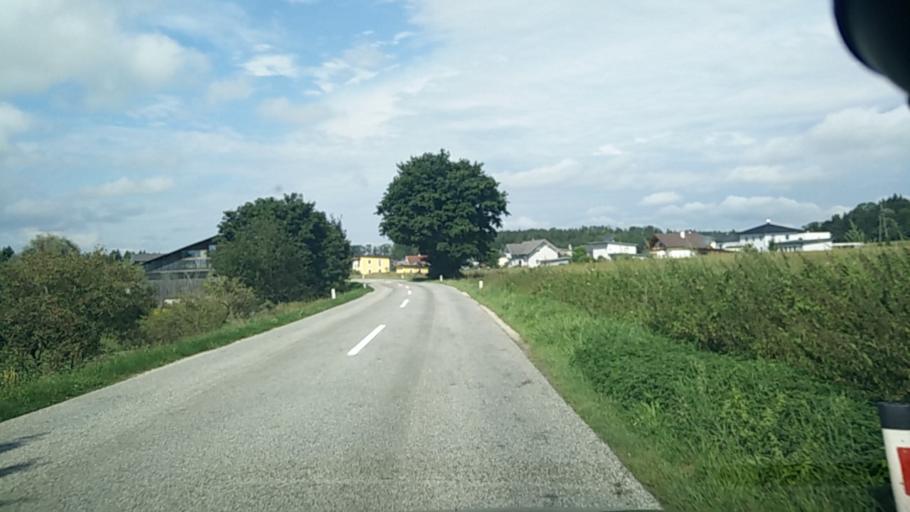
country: AT
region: Carinthia
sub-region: Politischer Bezirk Klagenfurt Land
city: Grafenstein
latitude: 46.6180
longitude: 14.5111
